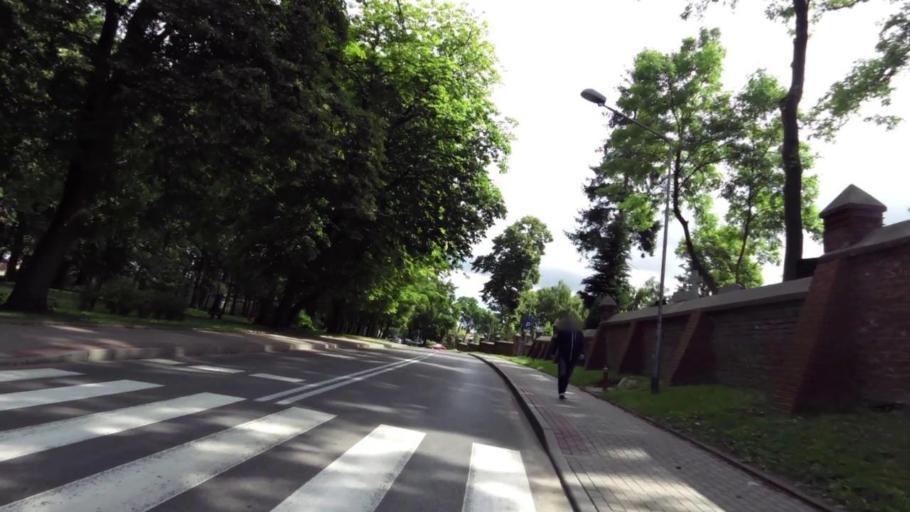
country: PL
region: West Pomeranian Voivodeship
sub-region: Powiat slawienski
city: Darlowo
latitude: 54.4249
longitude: 16.4153
